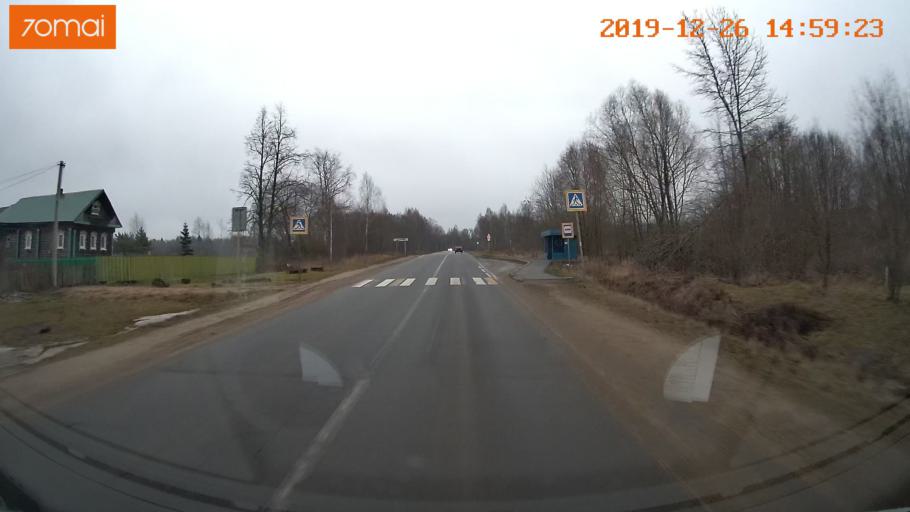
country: RU
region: Jaroslavl
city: Rybinsk
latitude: 58.2593
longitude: 38.8475
